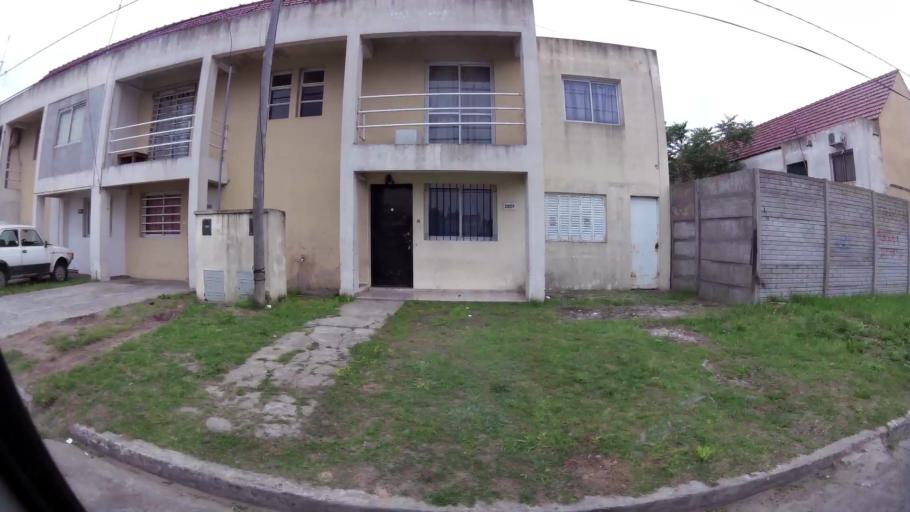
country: AR
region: Buenos Aires
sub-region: Partido de La Plata
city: La Plata
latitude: -34.9047
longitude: -57.9889
